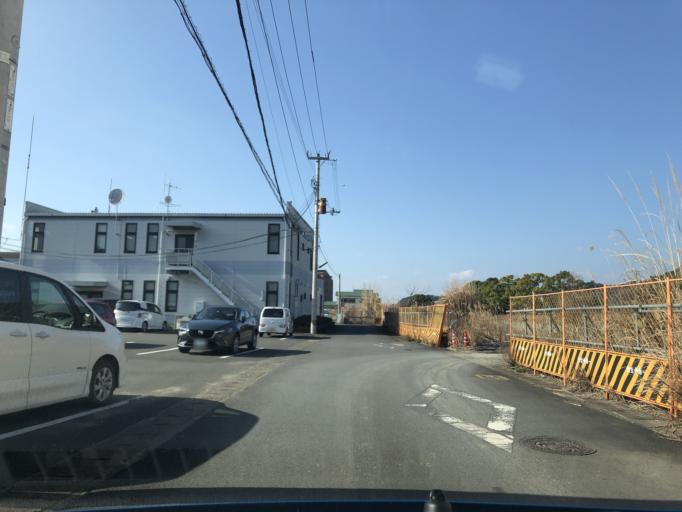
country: JP
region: Kochi
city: Sukumo
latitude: 32.9380
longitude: 132.7219
